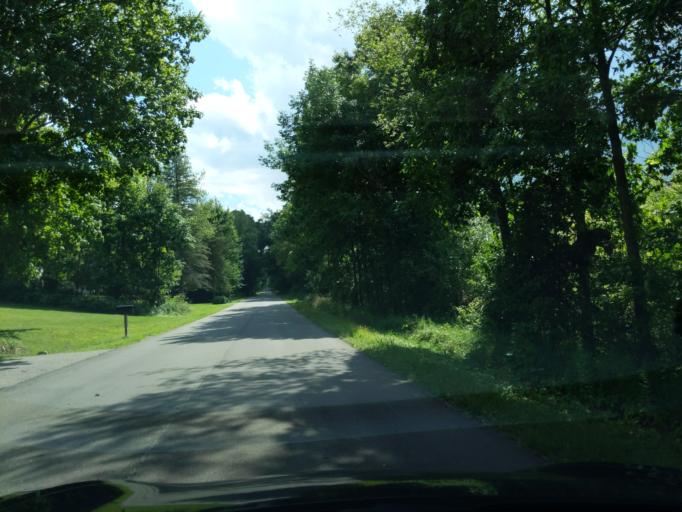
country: US
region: Michigan
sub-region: Eaton County
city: Eaton Rapids
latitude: 42.4778
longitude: -84.5807
